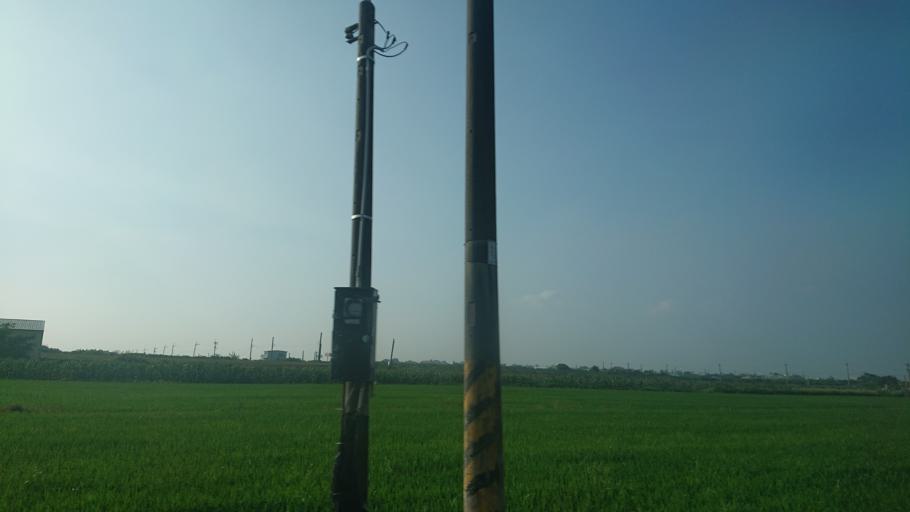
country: TW
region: Taiwan
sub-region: Tainan
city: Tainan
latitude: 23.1420
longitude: 120.2444
